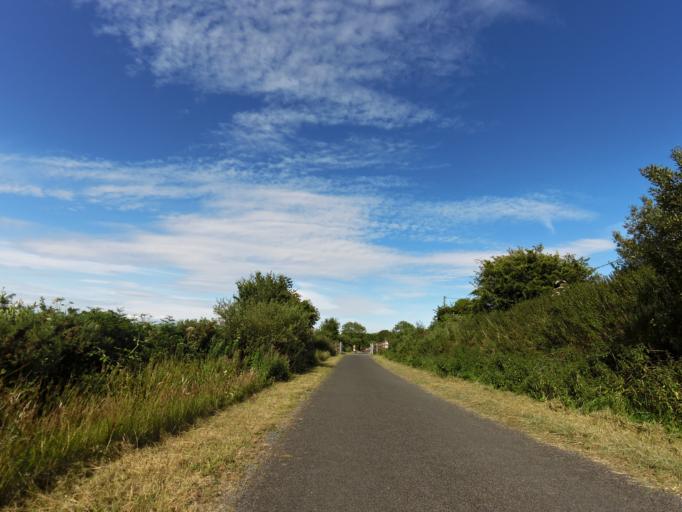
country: IE
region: Munster
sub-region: Waterford
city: Portlaw
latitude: 52.2178
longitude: -7.3521
